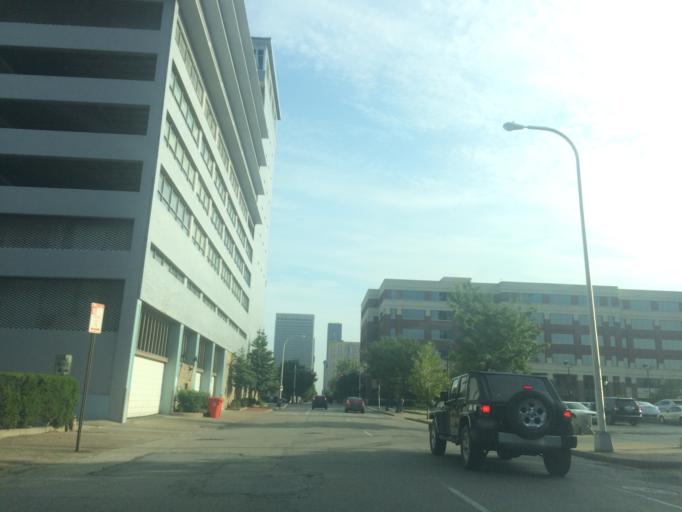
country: US
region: Kentucky
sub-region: Jefferson County
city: Louisville
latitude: 38.2453
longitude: -85.7603
